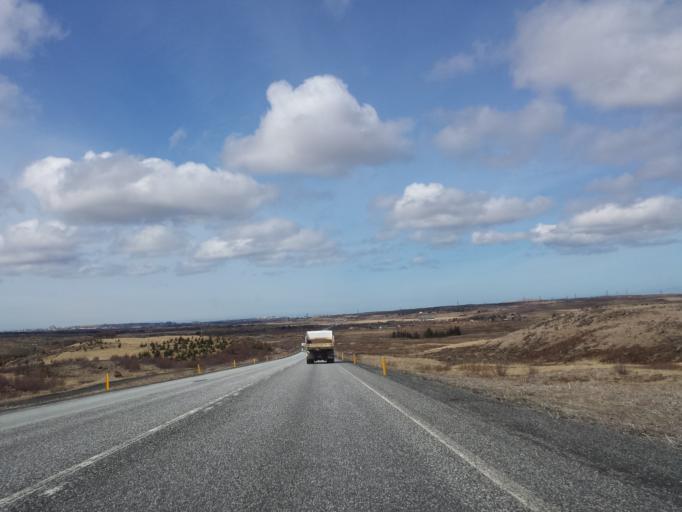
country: IS
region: Capital Region
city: Mosfellsbaer
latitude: 64.0765
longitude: -21.6506
